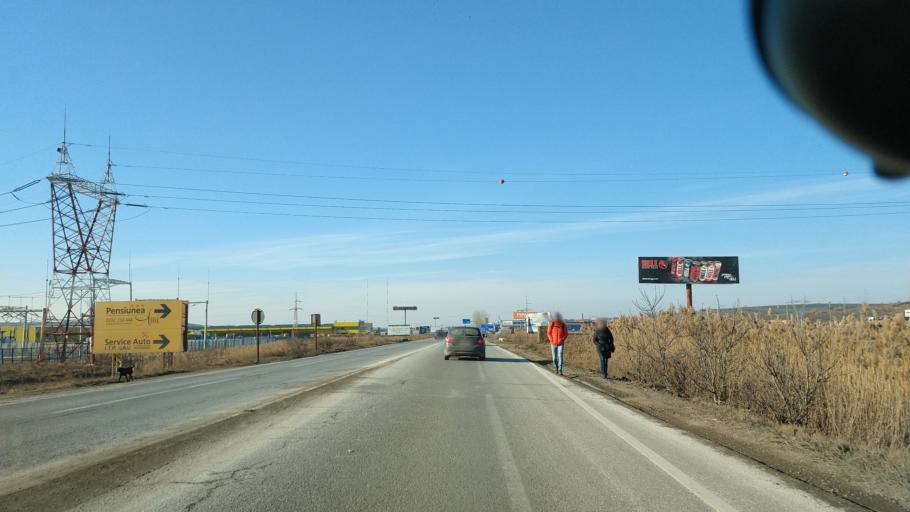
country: RO
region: Iasi
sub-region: Comuna Valea Lupului
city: Valea Lupului
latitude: 47.1790
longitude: 27.4818
